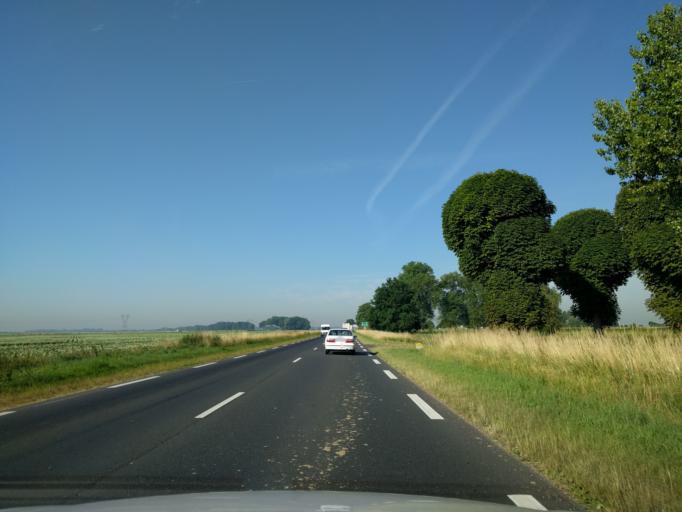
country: FR
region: Picardie
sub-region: Departement de la Somme
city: Roye
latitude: 49.6736
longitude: 2.7648
